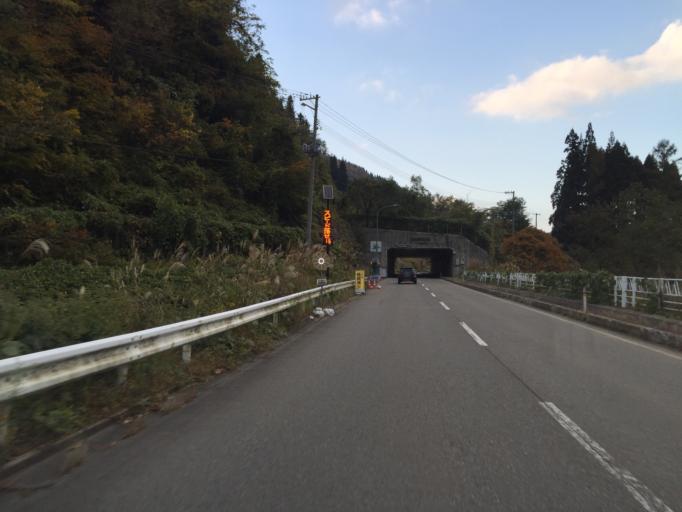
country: JP
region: Yamagata
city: Yonezawa
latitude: 37.8283
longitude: 140.0034
